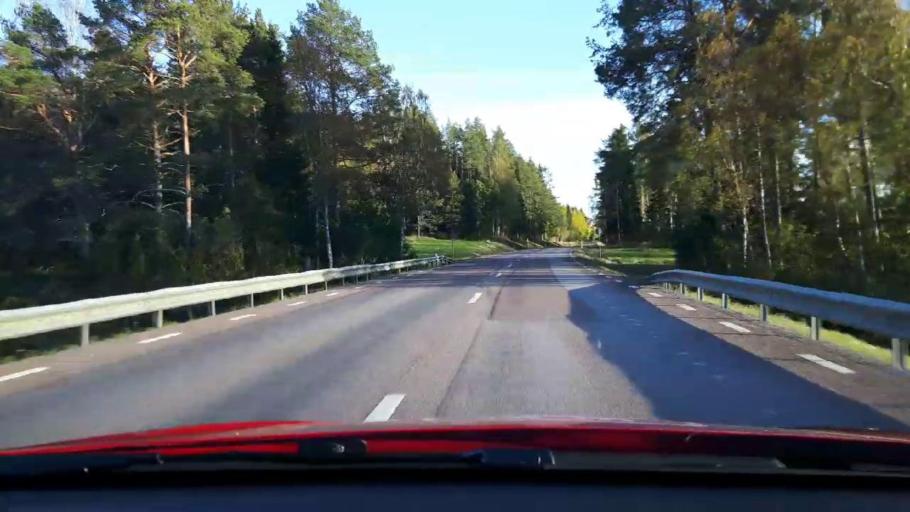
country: SE
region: Jaemtland
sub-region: OEstersunds Kommun
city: Brunflo
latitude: 63.0087
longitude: 14.9566
